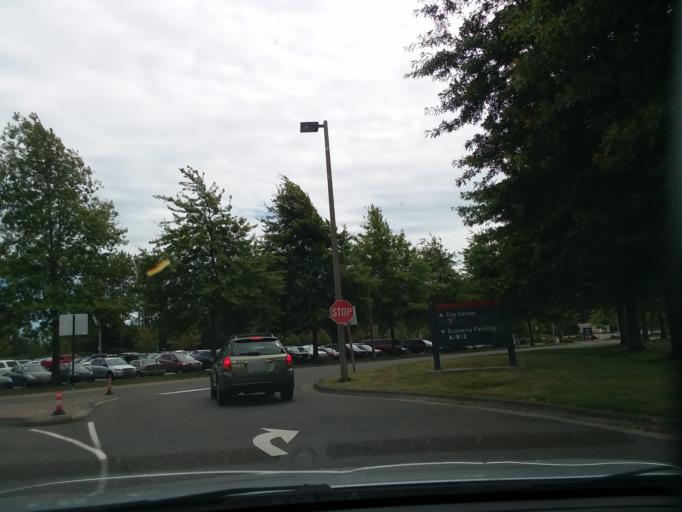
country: US
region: Washington
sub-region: Whatcom County
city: Marietta-Alderwood
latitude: 48.7943
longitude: -122.5310
